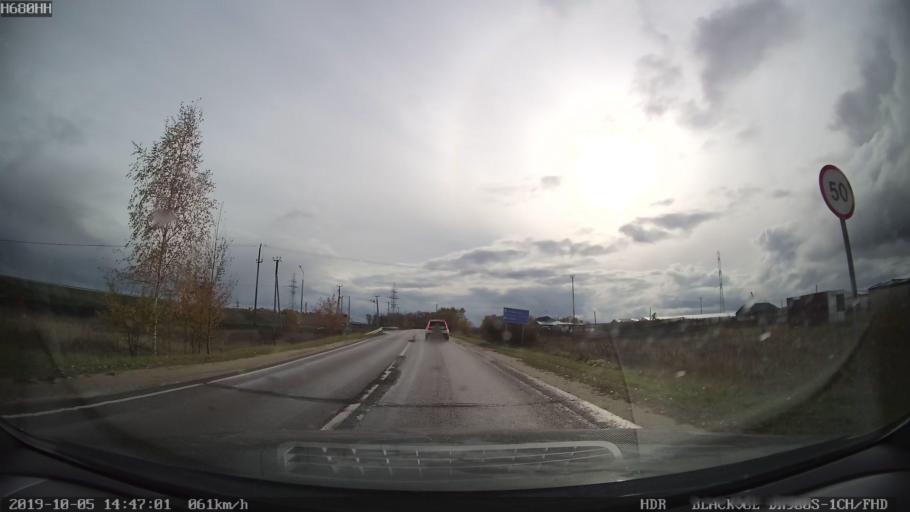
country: RU
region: Moskovskaya
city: Solnechnogorsk
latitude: 56.2220
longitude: 36.9046
